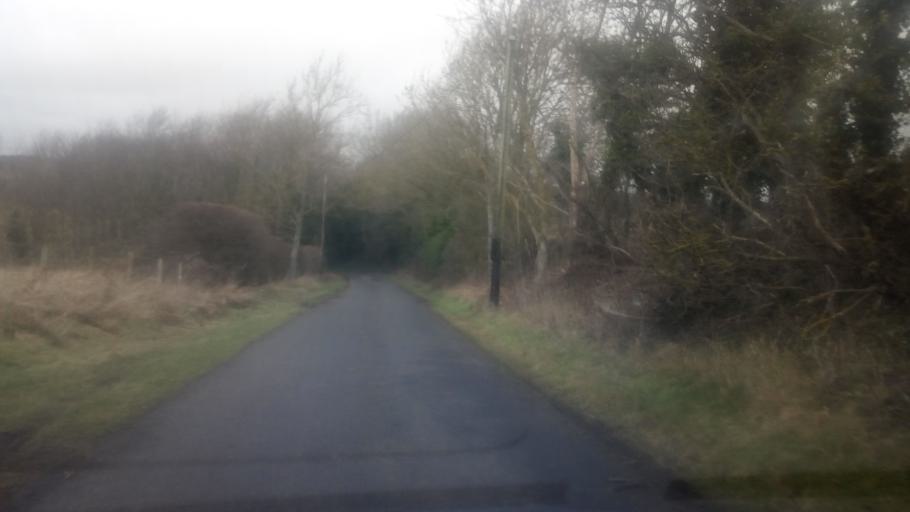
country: GB
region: Scotland
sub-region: The Scottish Borders
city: Kelso
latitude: 55.5726
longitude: -2.5158
